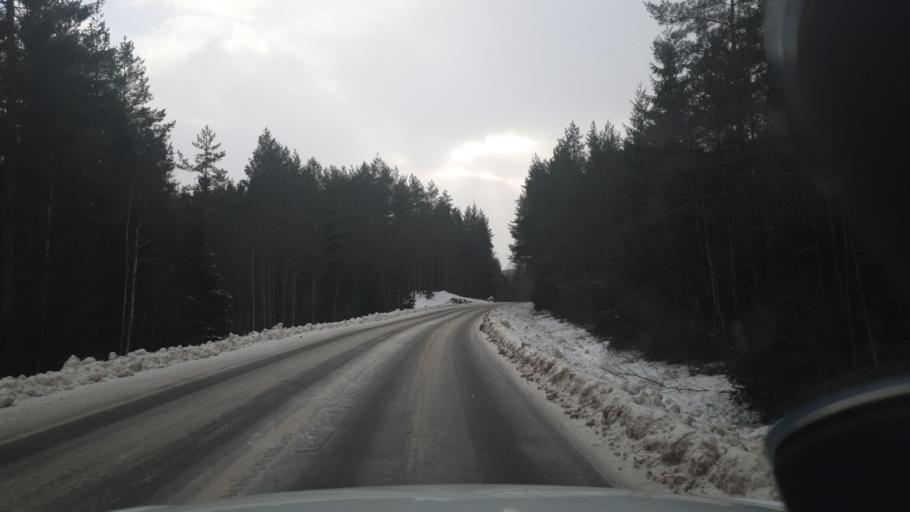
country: SE
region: Vaermland
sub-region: Eda Kommun
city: Amotfors
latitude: 59.5881
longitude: 12.2962
